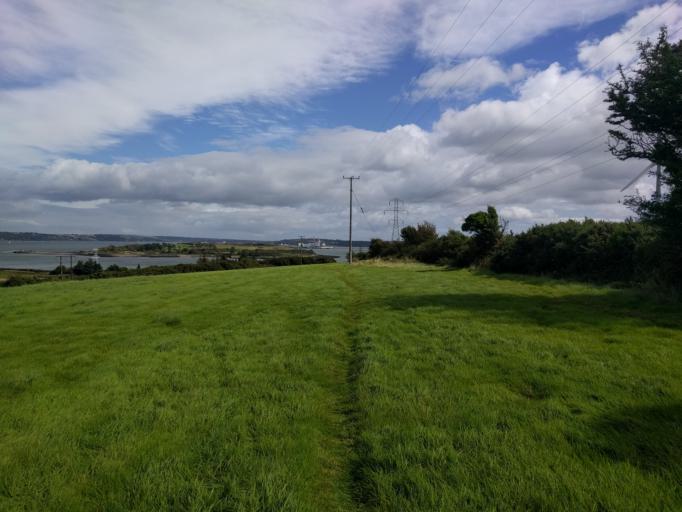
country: IE
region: Munster
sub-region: County Cork
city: Cobh
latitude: 51.8292
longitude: -8.3087
